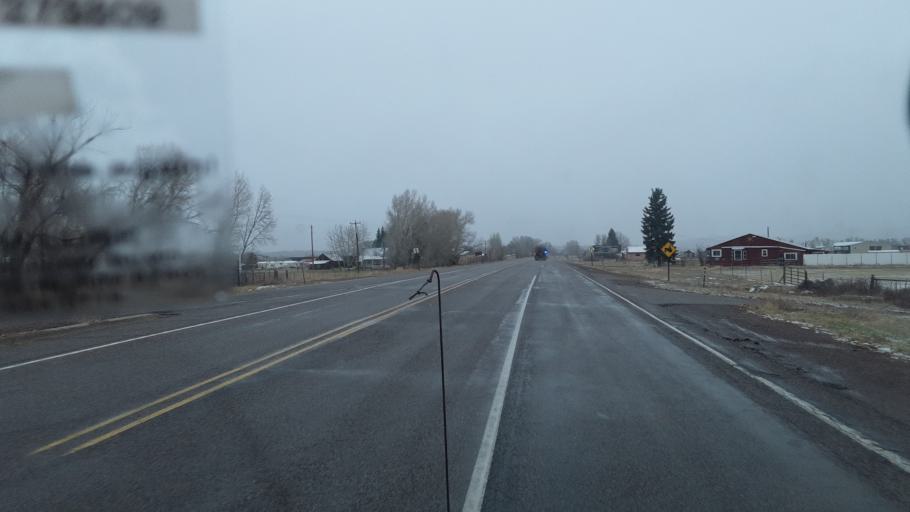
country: US
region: New Mexico
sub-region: Rio Arriba County
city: Tierra Amarilla
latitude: 36.7378
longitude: -106.5684
